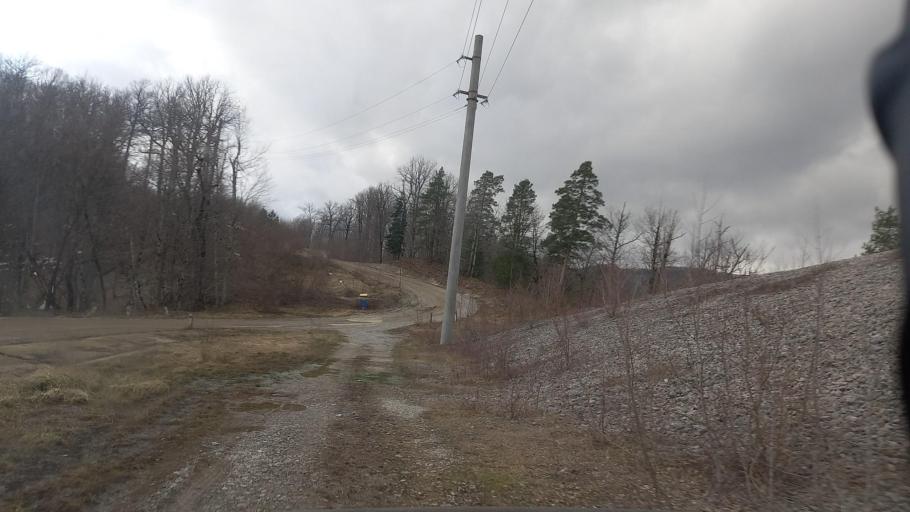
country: RU
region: Krasnodarskiy
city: Dzhubga
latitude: 44.5239
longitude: 38.7725
